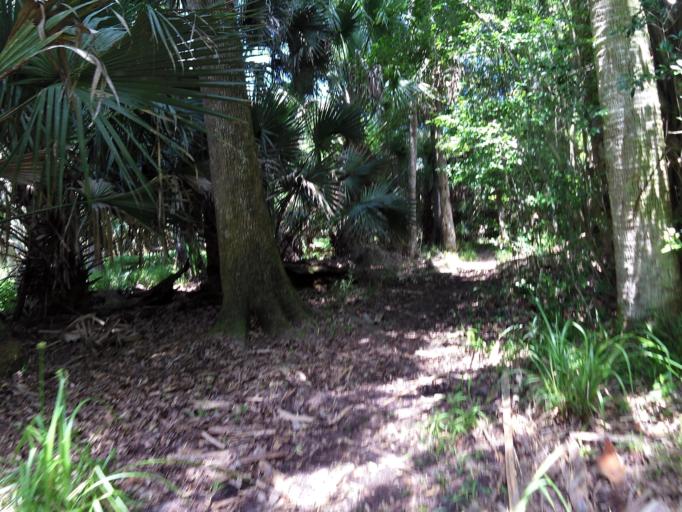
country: US
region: Florida
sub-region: Flagler County
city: Flagler Beach
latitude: 29.4208
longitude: -81.1377
